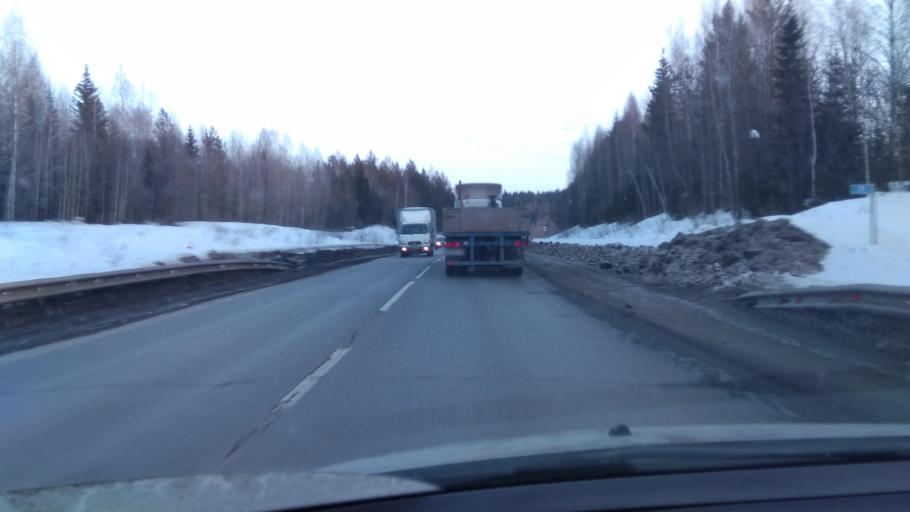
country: RU
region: Perm
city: Kukushtan
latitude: 57.5947
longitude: 56.5392
